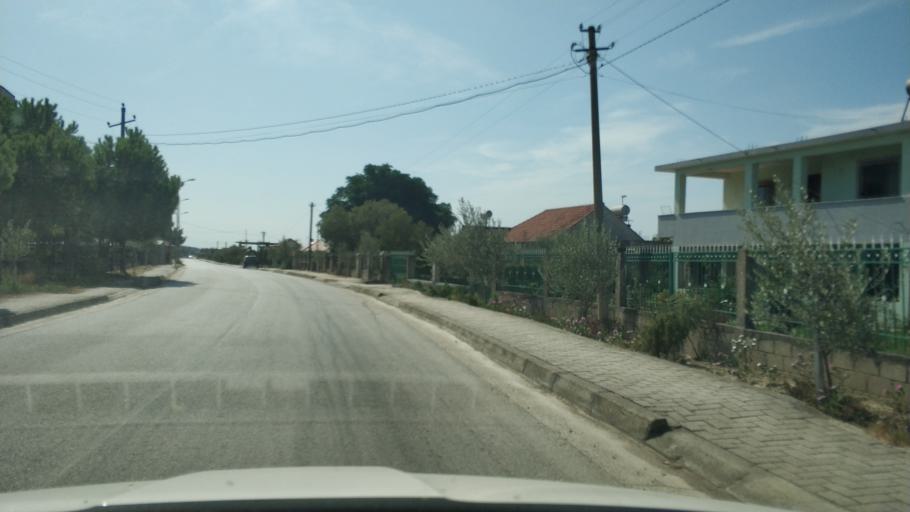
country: AL
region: Fier
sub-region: Rrethi i Lushnjes
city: Divjake
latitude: 40.9775
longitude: 19.5355
